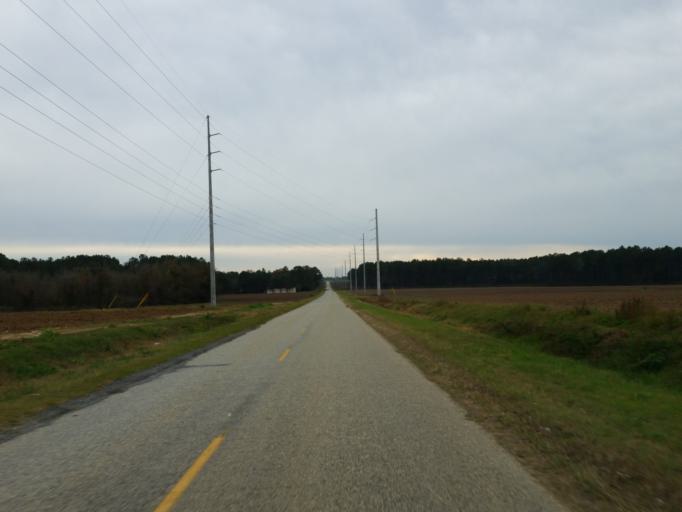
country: US
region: Georgia
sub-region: Dooly County
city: Vienna
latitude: 32.1414
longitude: -83.7611
